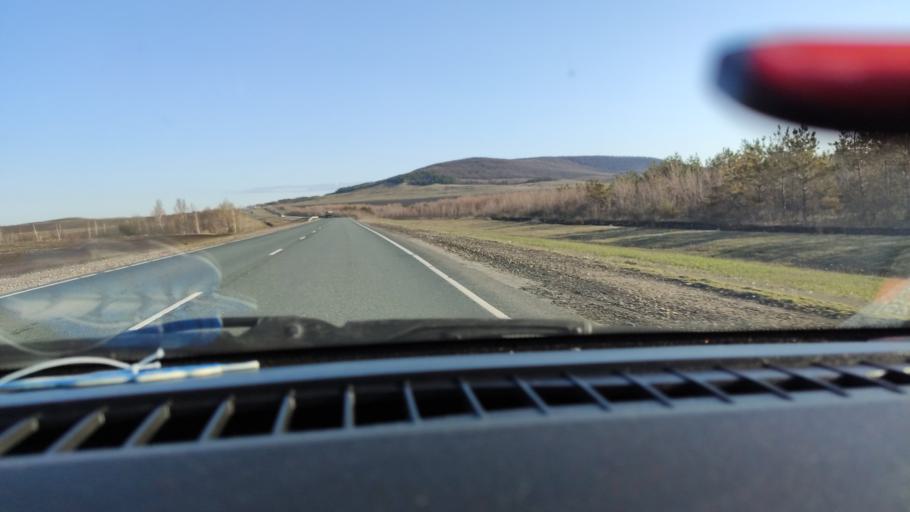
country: RU
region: Saratov
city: Alekseyevka
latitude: 52.2809
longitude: 47.9318
